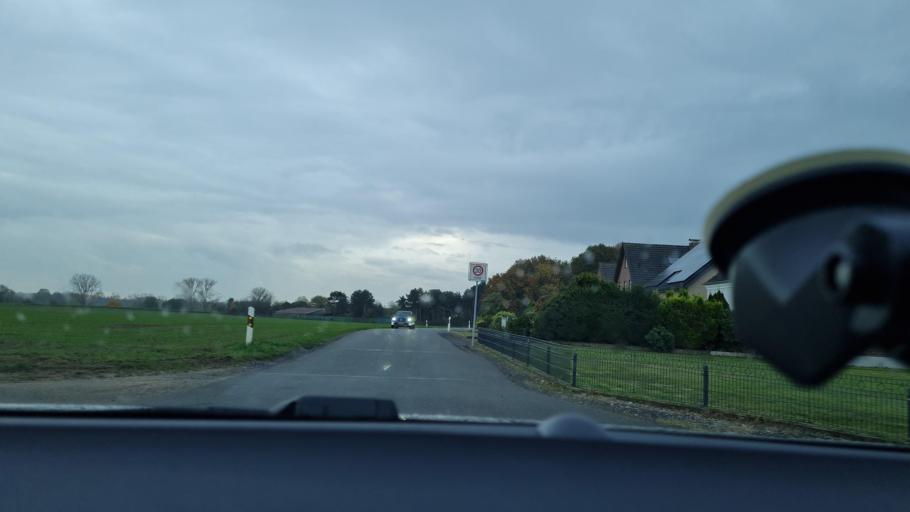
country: DE
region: North Rhine-Westphalia
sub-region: Regierungsbezirk Dusseldorf
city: Voerde
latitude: 51.6033
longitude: 6.6251
